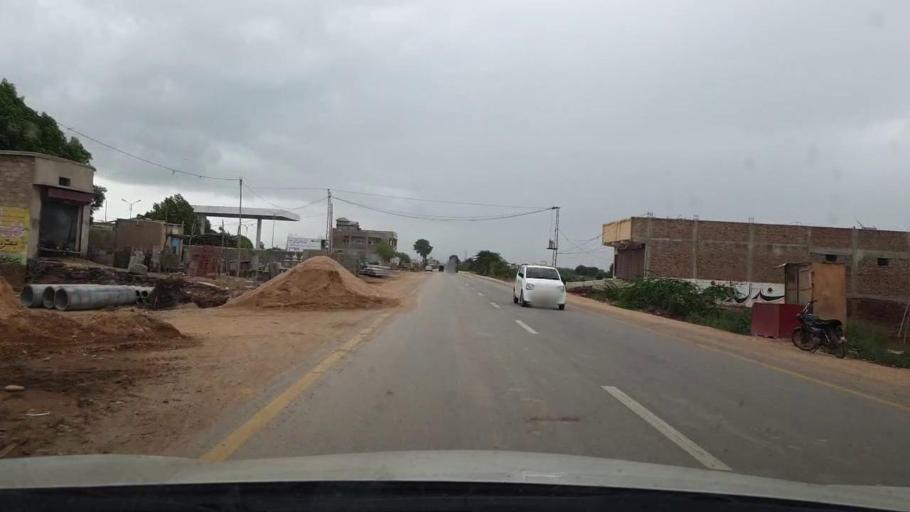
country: PK
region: Sindh
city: Kario
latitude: 24.6530
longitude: 68.5153
